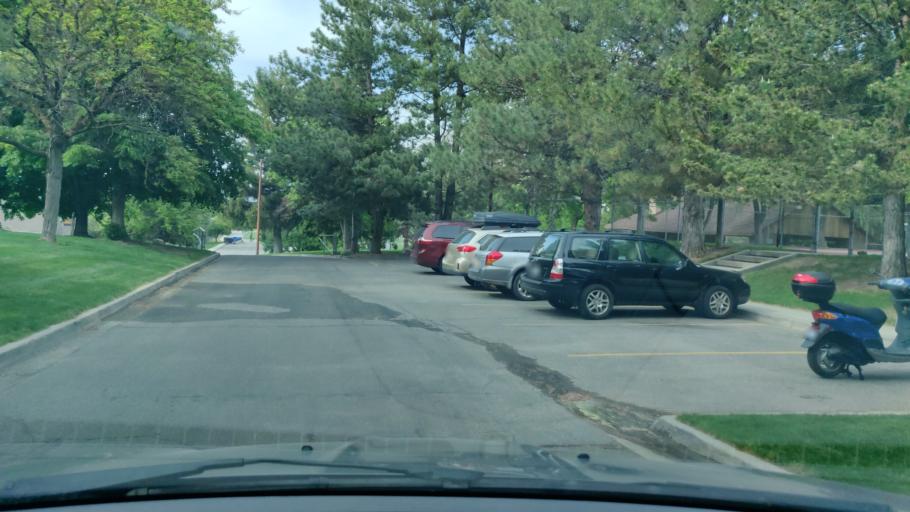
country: US
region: Utah
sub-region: Salt Lake County
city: Cottonwood Heights
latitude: 40.6171
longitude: -111.8055
